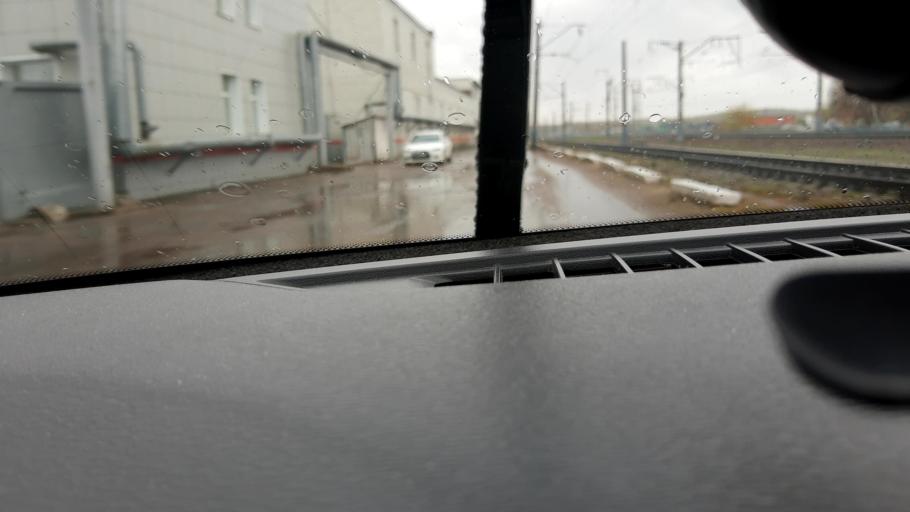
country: RU
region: Nizjnij Novgorod
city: Gorbatovka
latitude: 56.2852
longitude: 43.8513
